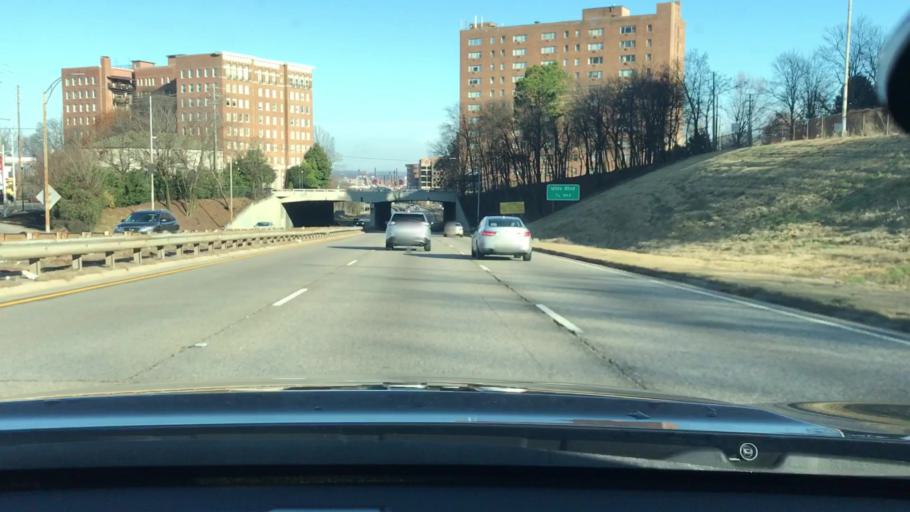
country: US
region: Alabama
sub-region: Jefferson County
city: Birmingham
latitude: 33.5011
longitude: -86.7892
